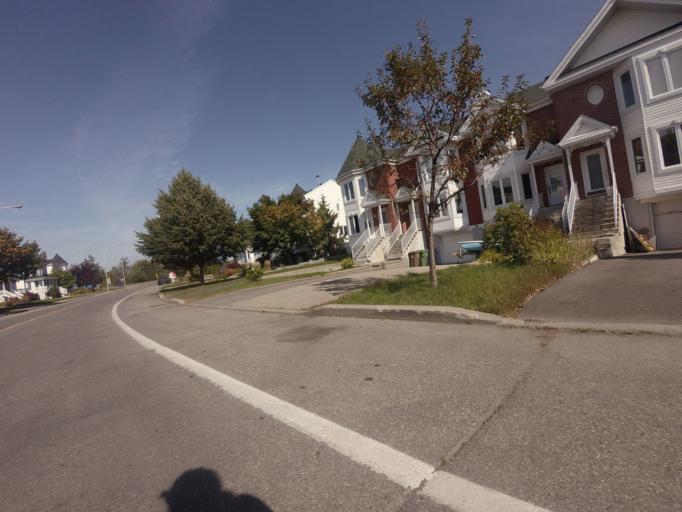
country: CA
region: Quebec
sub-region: Laurentides
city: Saint-Eustache
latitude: 45.5752
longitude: -73.9226
